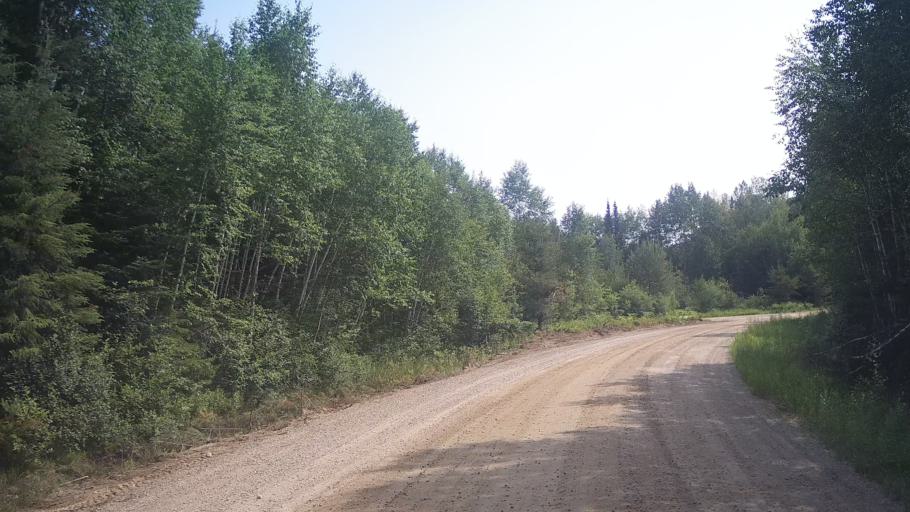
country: CA
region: Ontario
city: Timmins
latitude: 47.6776
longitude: -81.7204
